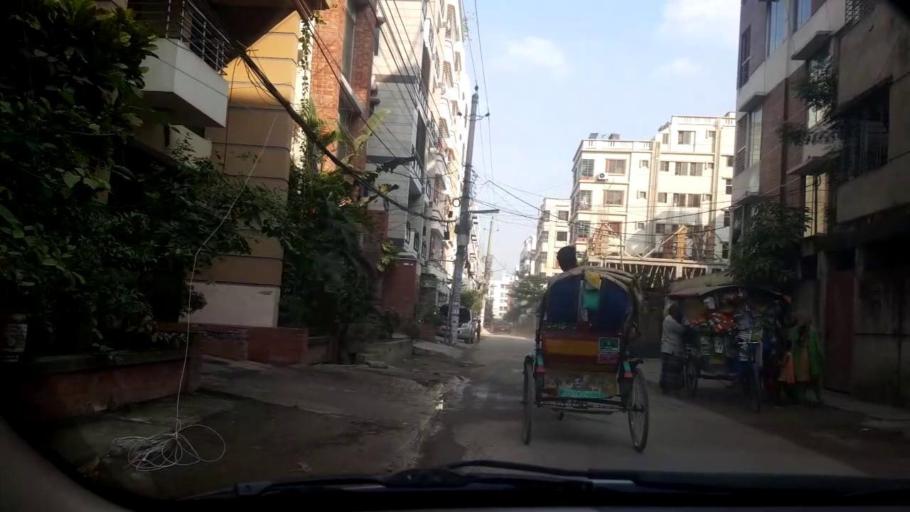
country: BD
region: Dhaka
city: Tungi
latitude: 23.8699
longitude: 90.3802
